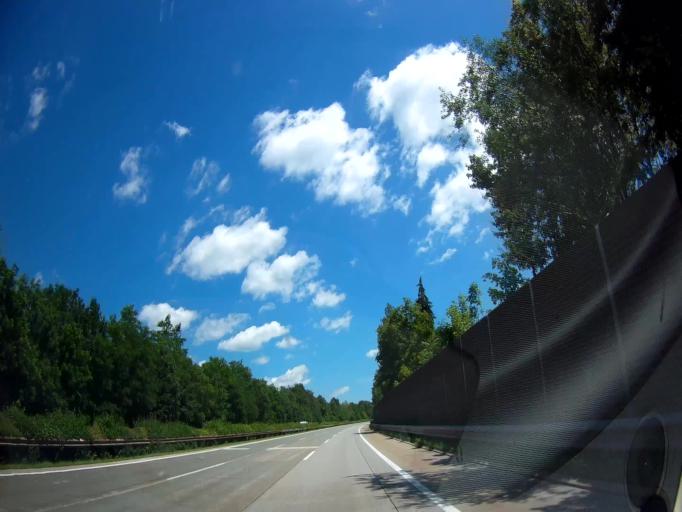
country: AT
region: Carinthia
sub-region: Politischer Bezirk Villach Land
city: Wernberg
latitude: 46.6235
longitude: 13.9198
